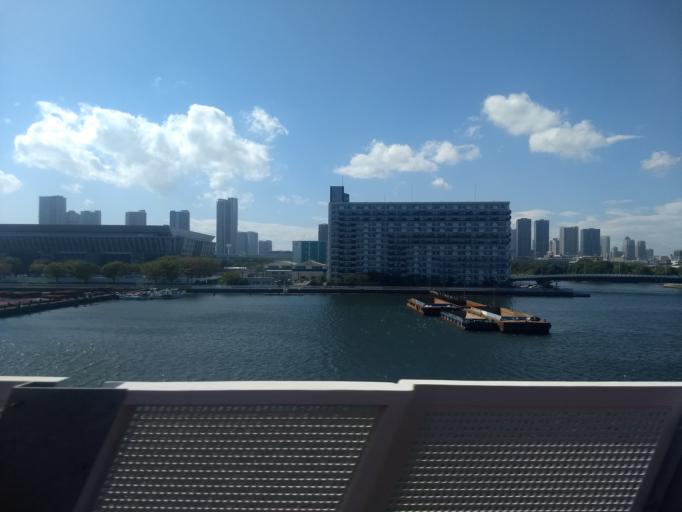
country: JP
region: Tokyo
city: Urayasu
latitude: 35.6535
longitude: 139.8194
